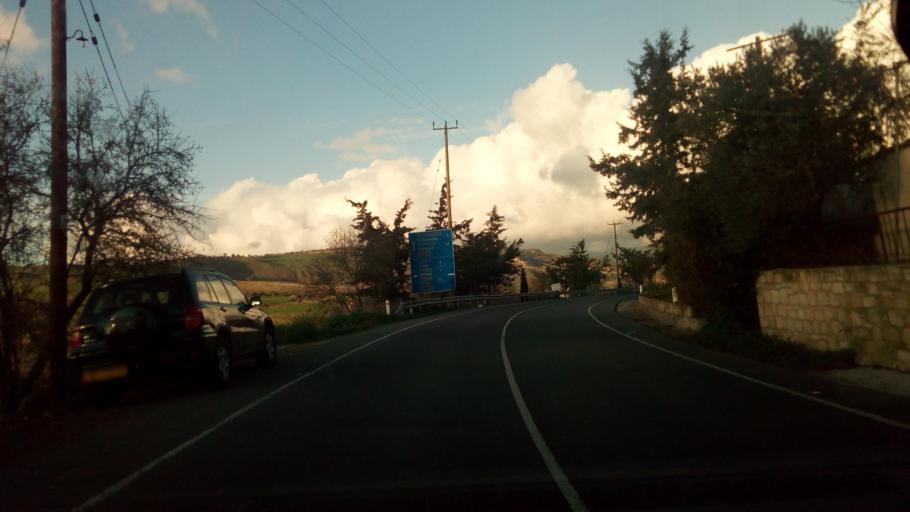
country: CY
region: Pafos
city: Mesogi
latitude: 34.9074
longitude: 32.5487
